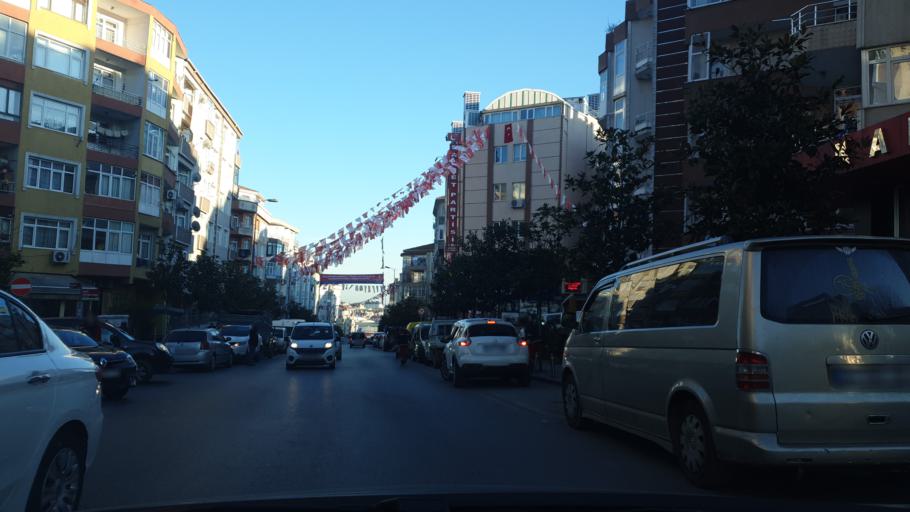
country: TR
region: Istanbul
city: merter keresteciler
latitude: 41.0204
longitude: 28.8736
